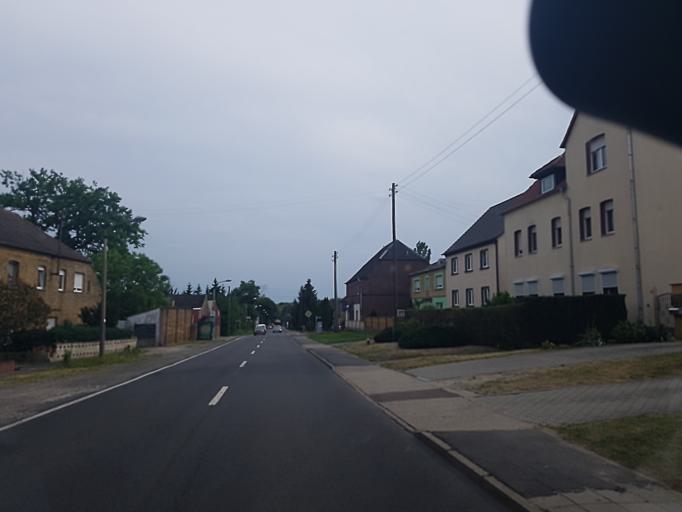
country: DE
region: Saxony-Anhalt
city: Nudersdorf
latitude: 51.9060
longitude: 12.6110
